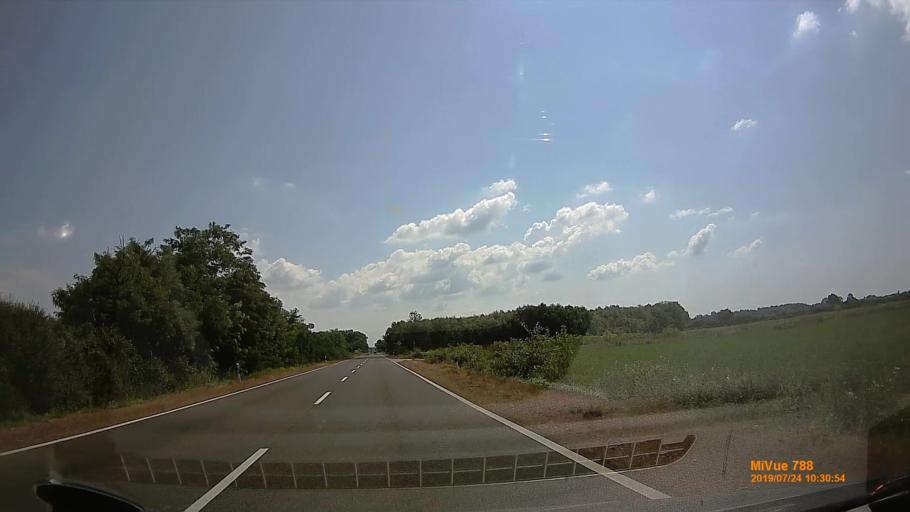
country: HU
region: Szabolcs-Szatmar-Bereg
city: Tarpa
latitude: 48.1606
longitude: 22.4998
